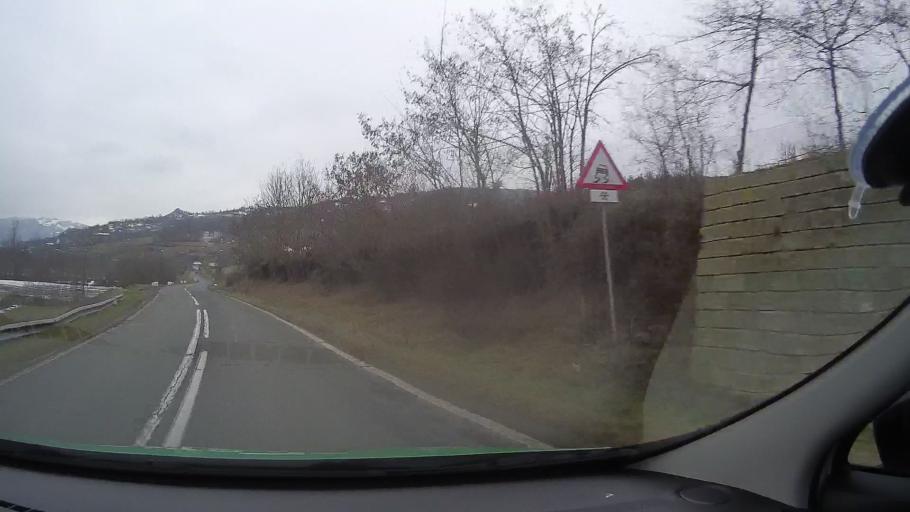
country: RO
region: Alba
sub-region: Comuna Metes
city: Metes
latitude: 46.1064
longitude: 23.4391
